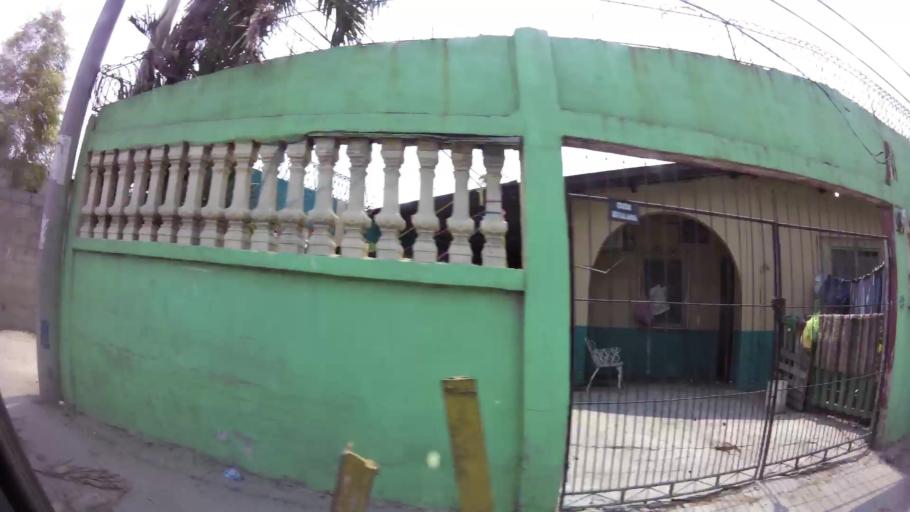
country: HN
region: Cortes
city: San Pedro Sula
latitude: 15.4898
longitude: -87.9900
